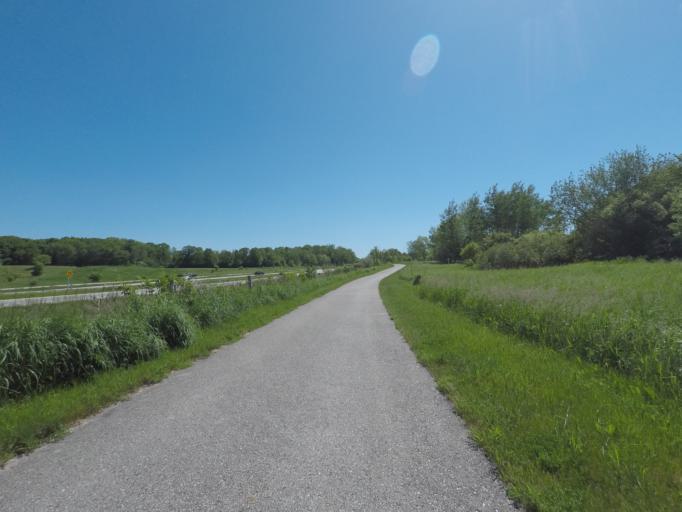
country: US
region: Wisconsin
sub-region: Sheboygan County
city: Kohler
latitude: 43.7528
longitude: -87.7781
